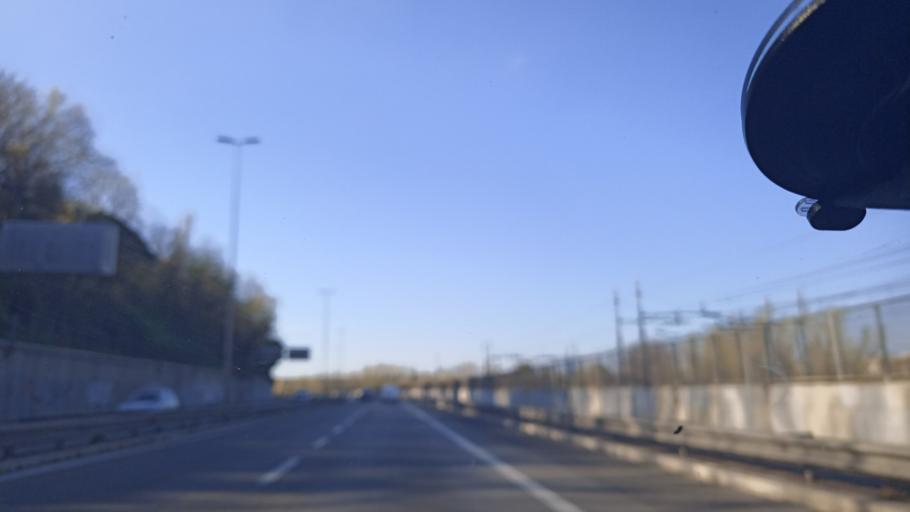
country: IT
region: Latium
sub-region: Citta metropolitana di Roma Capitale
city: Rome
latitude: 41.9358
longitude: 12.5204
